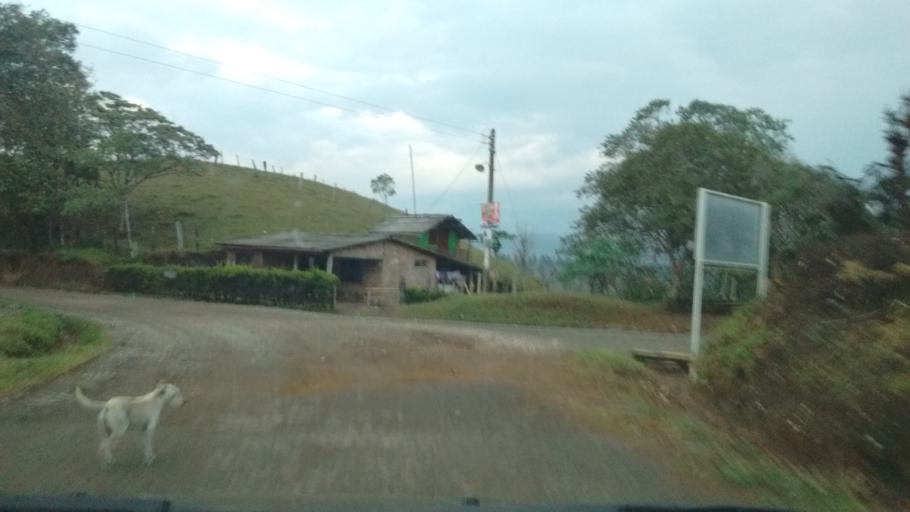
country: CO
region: Cauca
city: Lopez
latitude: 2.3780
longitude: -76.7170
